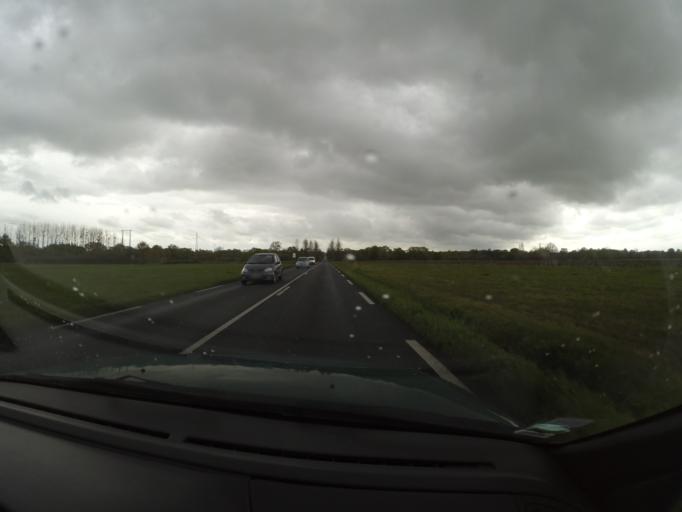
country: FR
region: Pays de la Loire
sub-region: Departement de la Loire-Atlantique
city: Vallet
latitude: 47.1945
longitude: -1.2499
